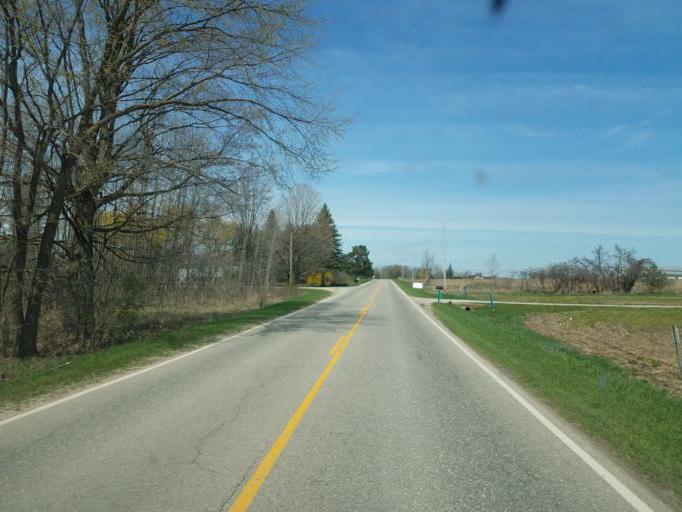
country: US
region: Michigan
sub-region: Clare County
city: Clare
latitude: 43.8218
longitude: -84.6667
